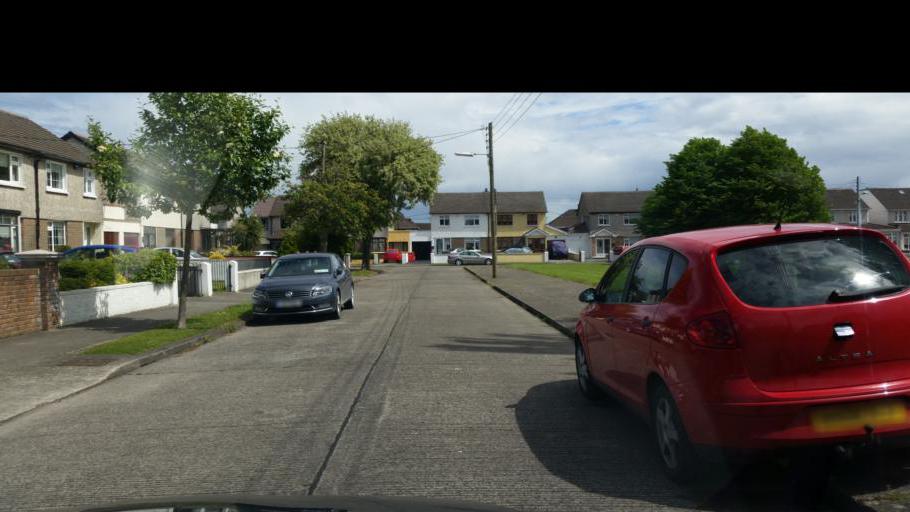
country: IE
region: Leinster
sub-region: Dublin City
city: Finglas
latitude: 53.3922
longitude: -6.2817
